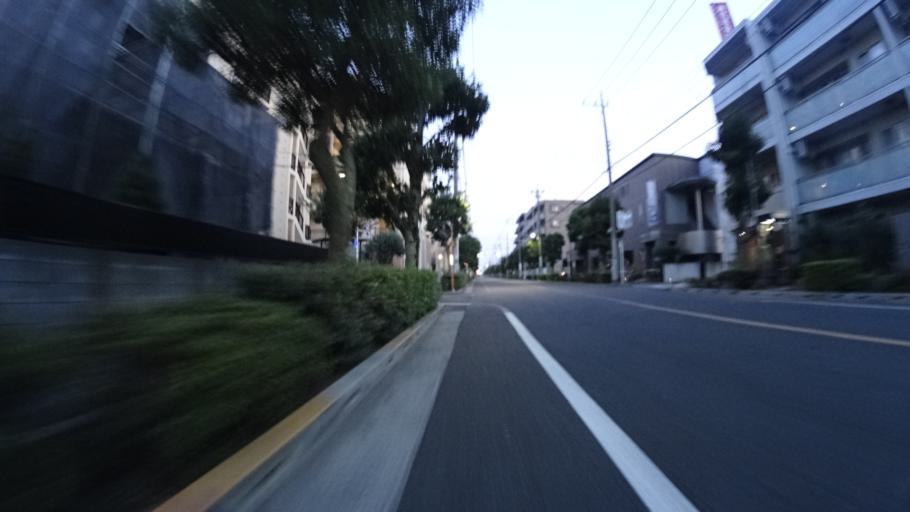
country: JP
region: Tokyo
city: Chofugaoka
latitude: 35.6525
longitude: 139.5338
